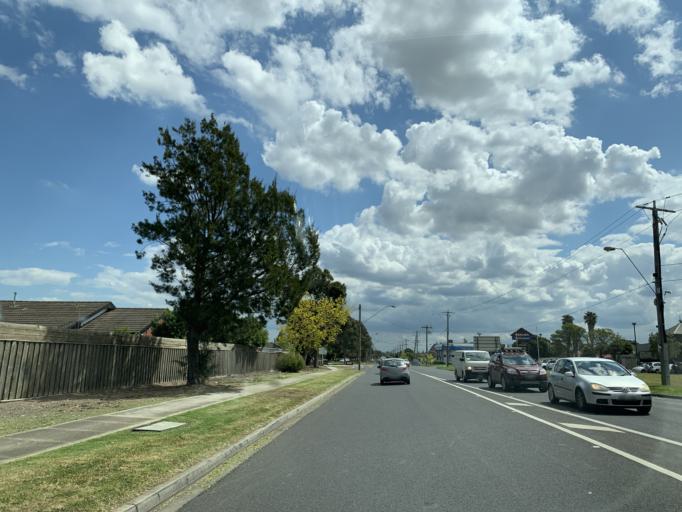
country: AU
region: Victoria
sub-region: Brimbank
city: Kealba
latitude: -37.7479
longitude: 144.8298
